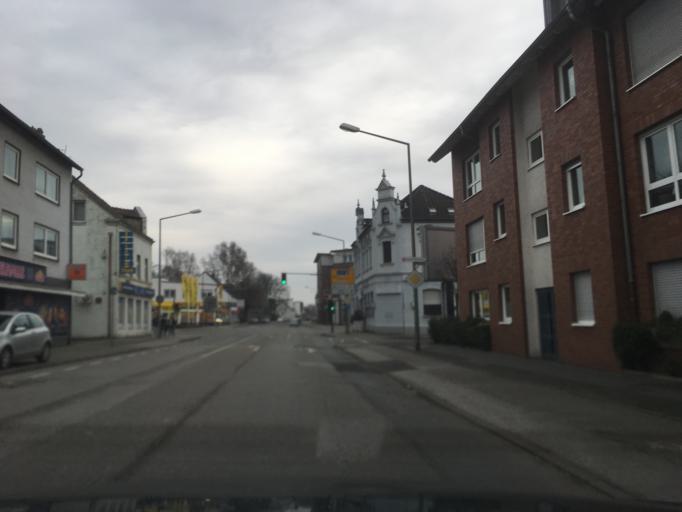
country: DE
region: North Rhine-Westphalia
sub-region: Regierungsbezirk Munster
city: Bottrop
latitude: 51.5332
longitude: 6.9551
